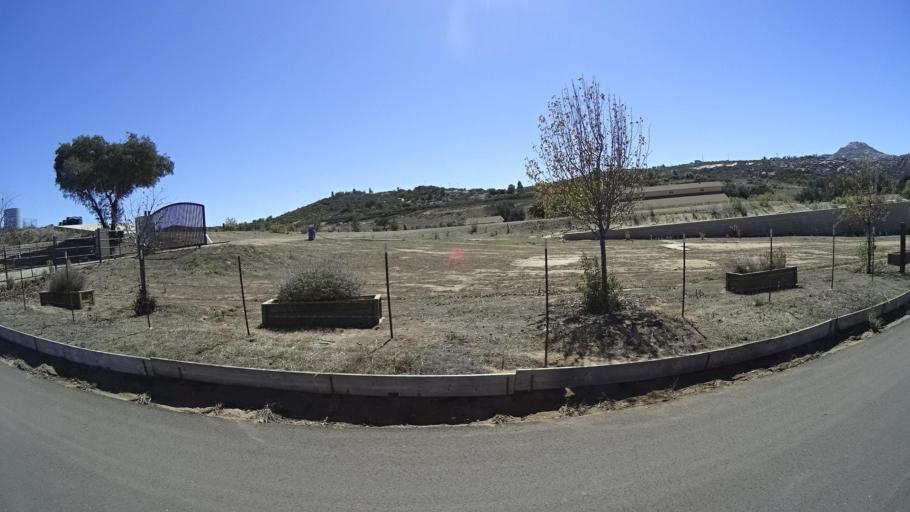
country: US
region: California
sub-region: San Diego County
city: Alpine
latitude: 32.7685
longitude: -116.6887
